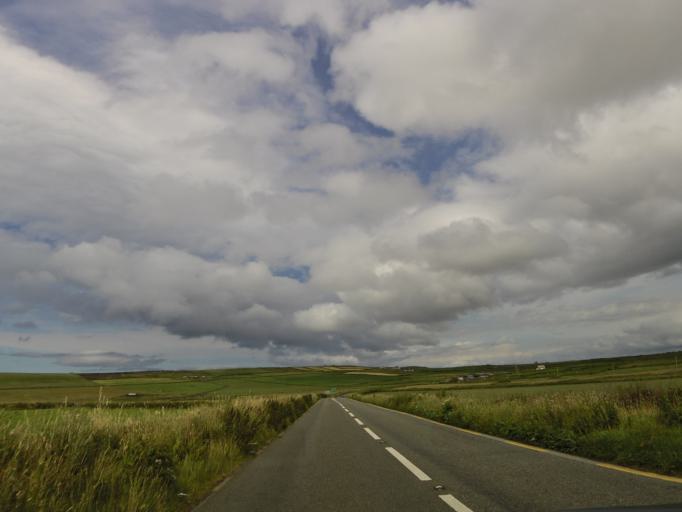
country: IE
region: Munster
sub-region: An Clar
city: Kilrush
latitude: 52.6885
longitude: -9.6407
